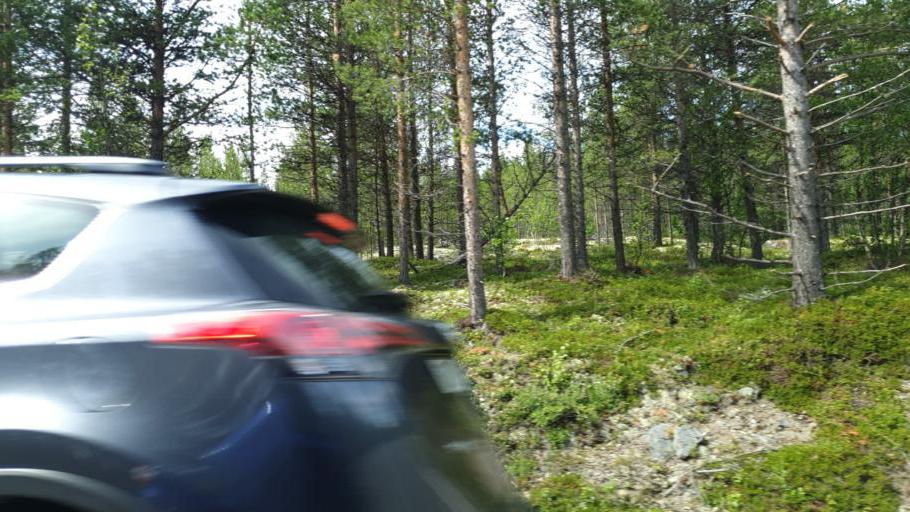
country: NO
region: Oppland
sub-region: Vaga
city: Vagamo
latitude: 61.6849
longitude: 9.0589
